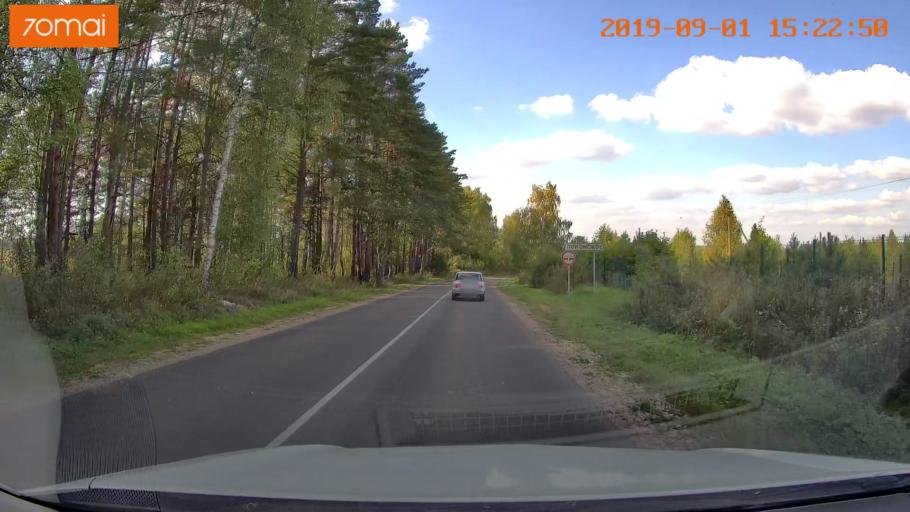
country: RU
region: Kaluga
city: Maloyaroslavets
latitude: 54.9397
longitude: 36.4606
